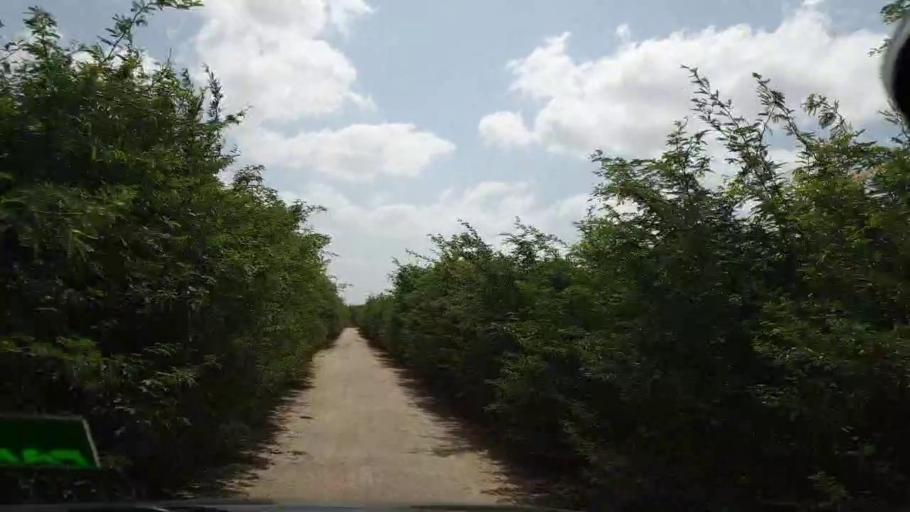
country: PK
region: Sindh
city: Kadhan
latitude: 24.5444
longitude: 69.2070
